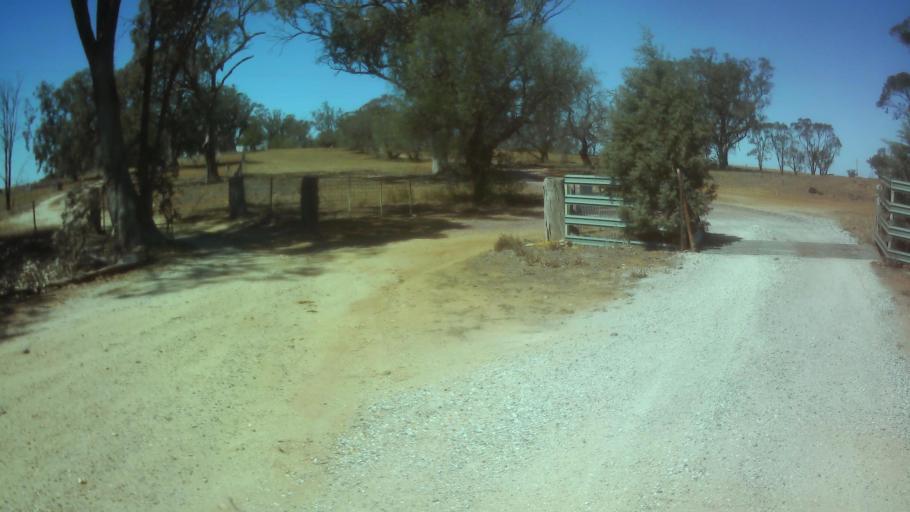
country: AU
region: New South Wales
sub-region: Cowra
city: Cowra
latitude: -33.8865
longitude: 148.4981
